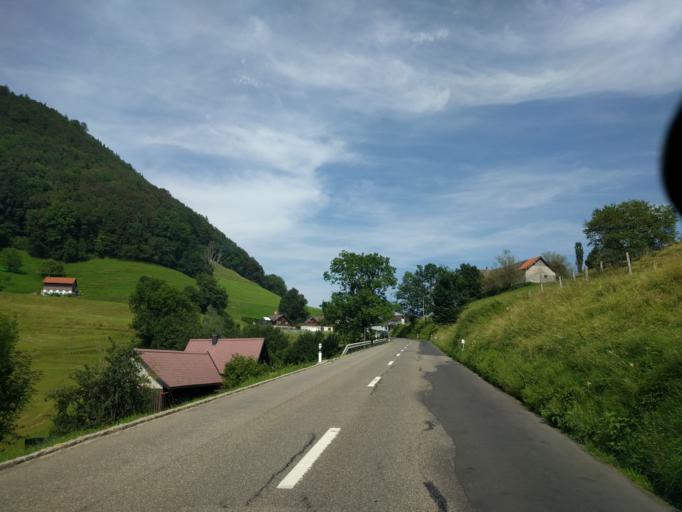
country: CH
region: Saint Gallen
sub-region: Wahlkreis Toggenburg
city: Lichtensteig
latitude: 47.3244
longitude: 9.1090
